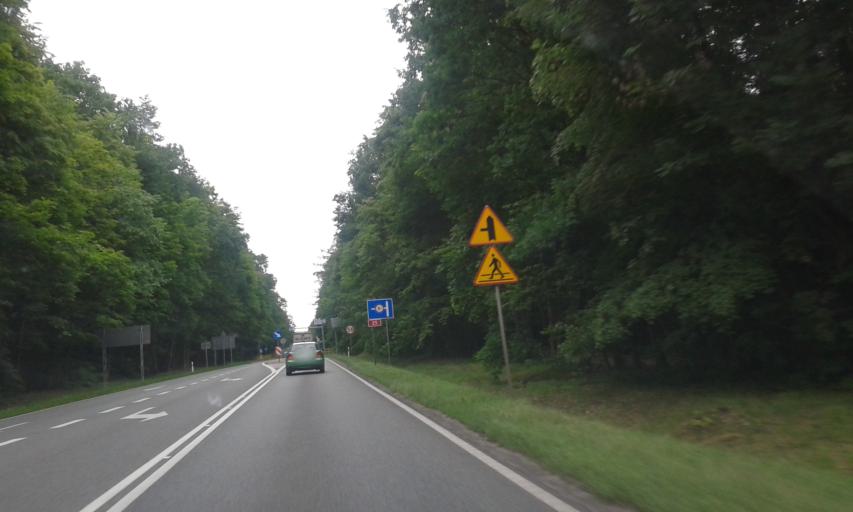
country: PL
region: Kujawsko-Pomorskie
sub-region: Powiat bydgoski
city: Biale Blota
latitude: 53.2010
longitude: 17.9285
